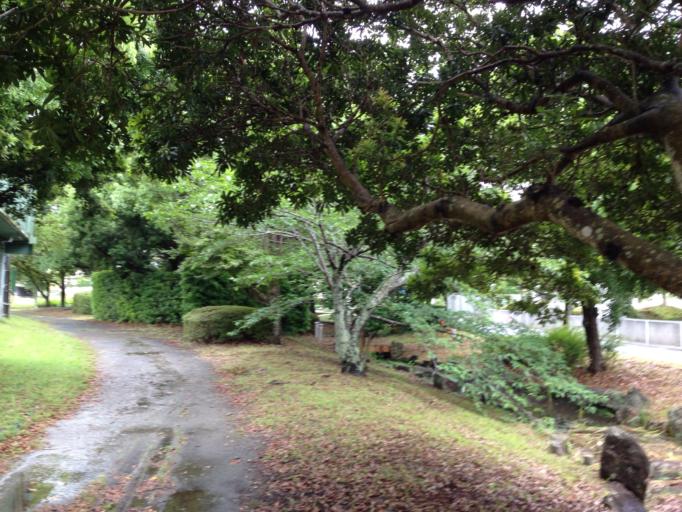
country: JP
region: Shizuoka
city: Fukuroi
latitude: 34.7440
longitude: 137.9457
